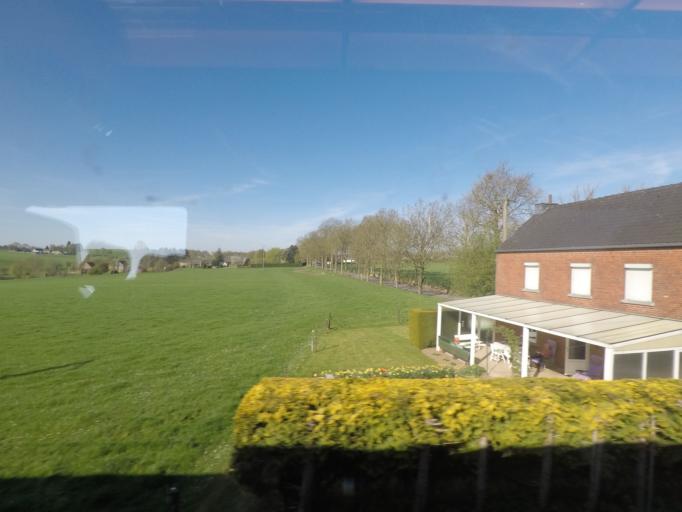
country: BE
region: Wallonia
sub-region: Province de Namur
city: Assesse
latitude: 50.3572
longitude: 5.0565
